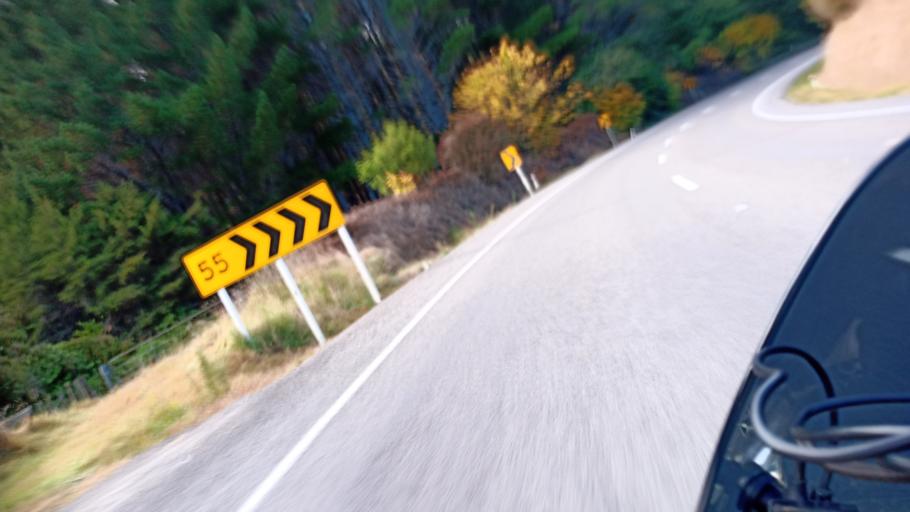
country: NZ
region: Gisborne
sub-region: Gisborne District
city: Gisborne
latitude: -38.8376
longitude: 177.8965
